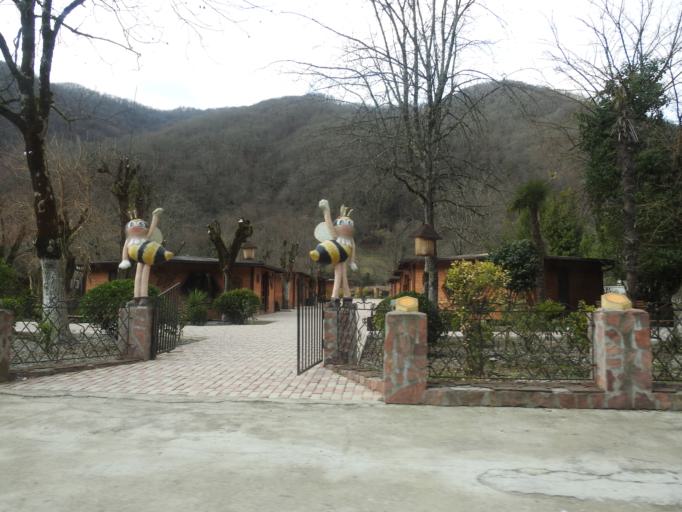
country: GE
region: Abkhazia
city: Gagra
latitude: 43.2828
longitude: 40.3981
